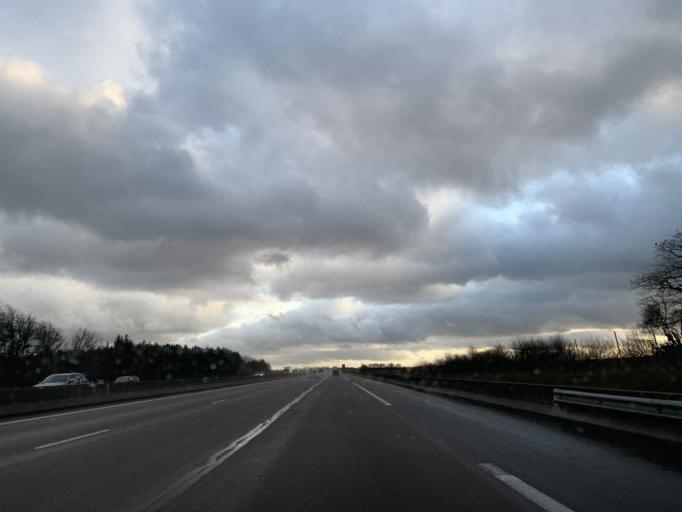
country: FR
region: Champagne-Ardenne
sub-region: Departement de la Haute-Marne
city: Langres
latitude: 47.8537
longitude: 5.2279
